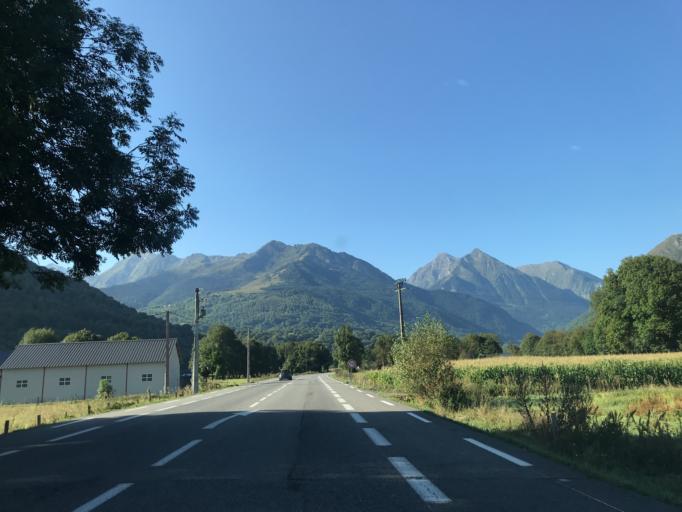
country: FR
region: Midi-Pyrenees
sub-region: Departement des Hautes-Pyrenees
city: Saint-Lary-Soulan
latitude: 42.8382
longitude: 0.3425
